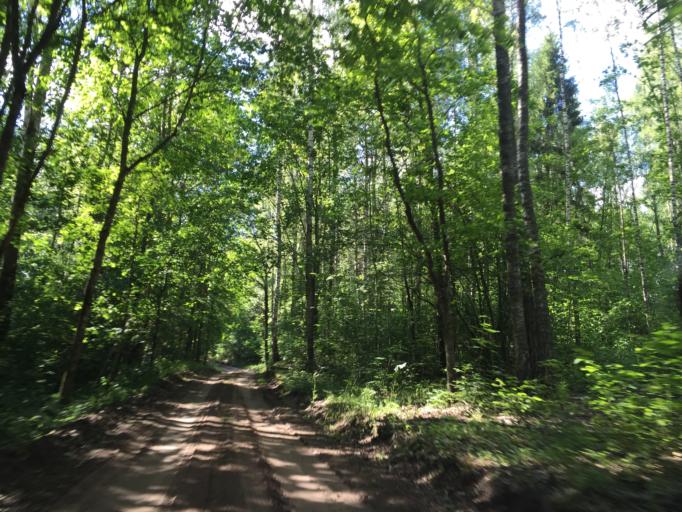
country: LV
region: Vecumnieki
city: Vecumnieki
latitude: 56.4383
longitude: 24.5911
